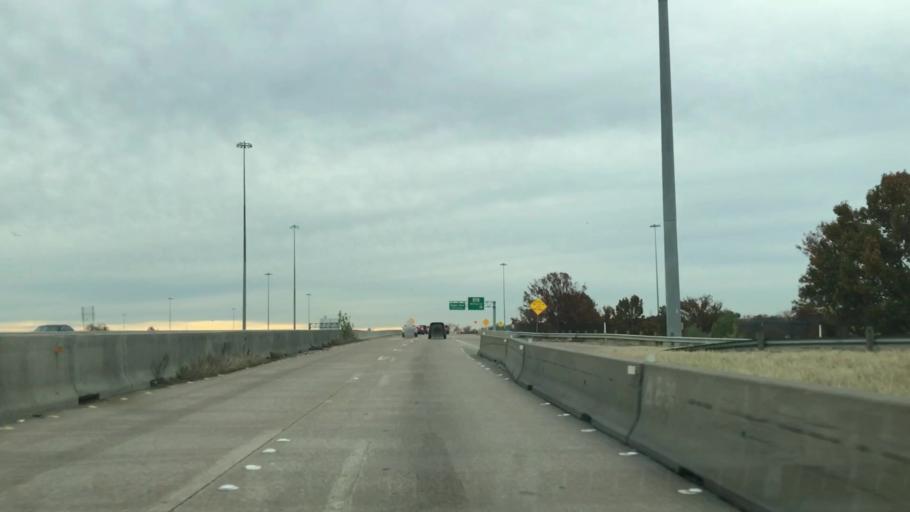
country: US
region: Texas
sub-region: Dallas County
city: Irving
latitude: 32.8398
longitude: -96.9063
